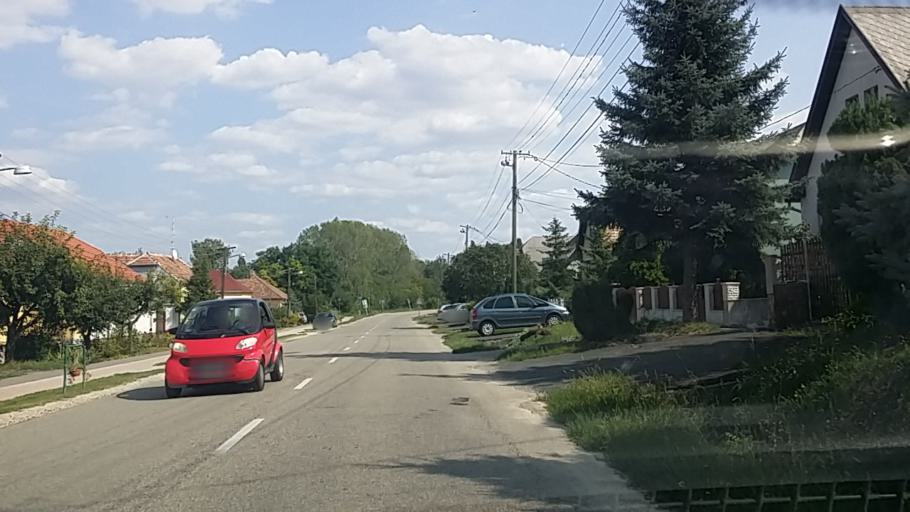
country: HU
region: Gyor-Moson-Sopron
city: Nagycenk
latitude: 47.6253
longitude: 16.7451
